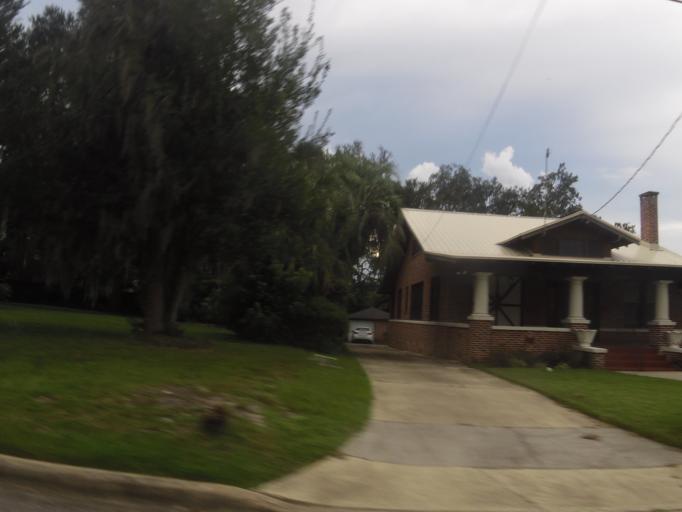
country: US
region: Florida
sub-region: Duval County
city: Jacksonville
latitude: 30.2893
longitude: -81.7174
